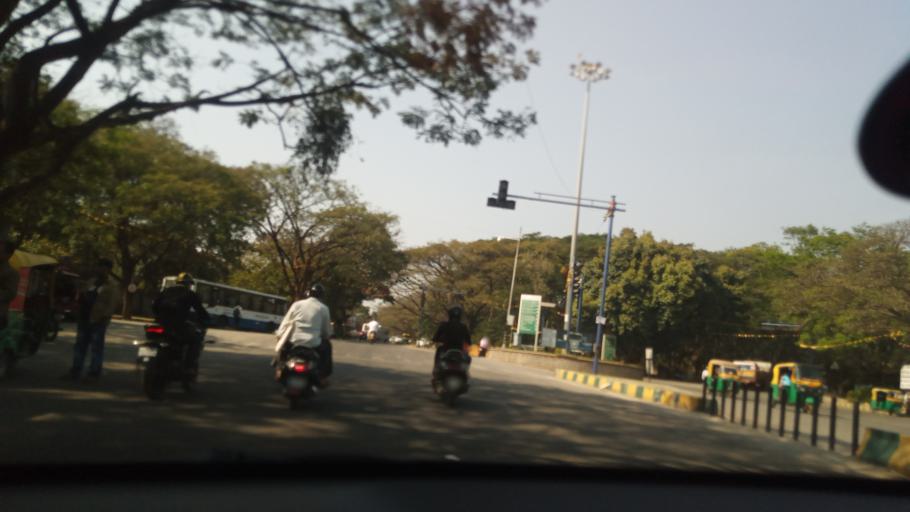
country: IN
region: Karnataka
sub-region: Bangalore Urban
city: Yelahanka
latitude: 13.0451
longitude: 77.5566
